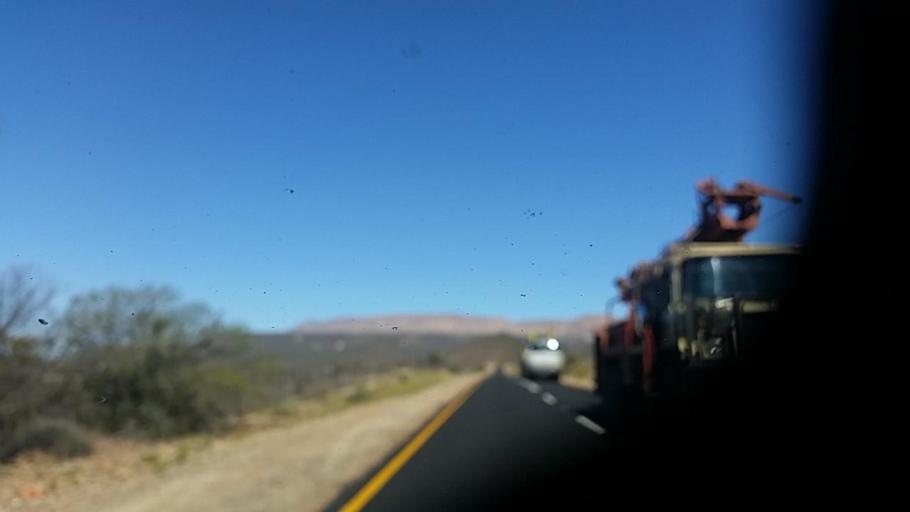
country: ZA
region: Western Cape
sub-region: Eden District Municipality
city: George
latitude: -33.5445
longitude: 22.7331
